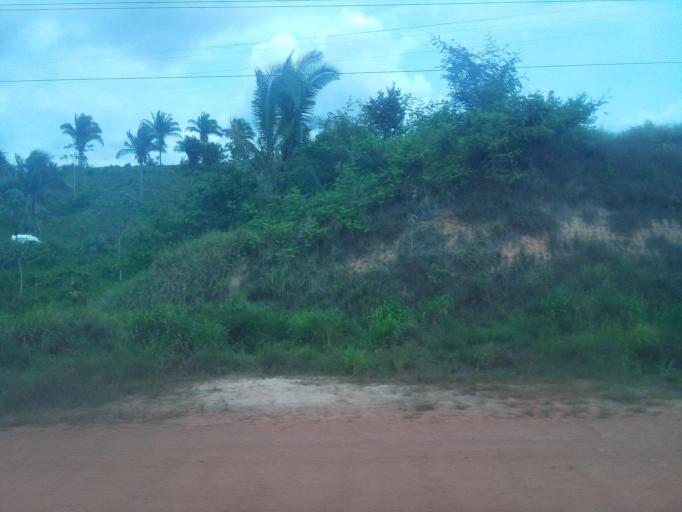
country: BR
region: Maranhao
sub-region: Santa Ines
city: Santa Ines
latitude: -3.7329
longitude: -46.1050
